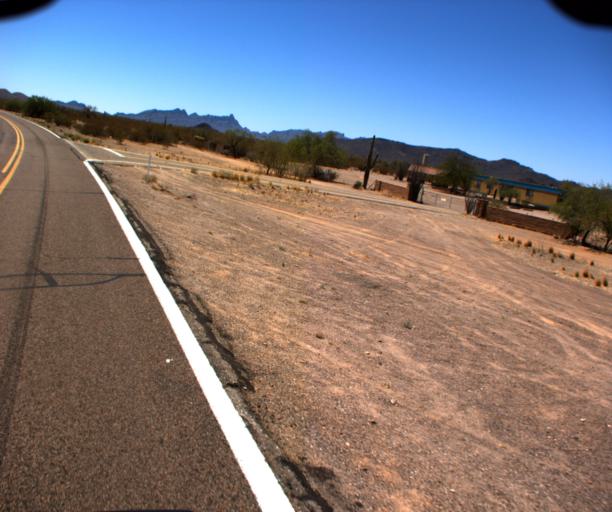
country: US
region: Arizona
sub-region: Pima County
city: Ajo
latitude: 32.2443
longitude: -112.7278
